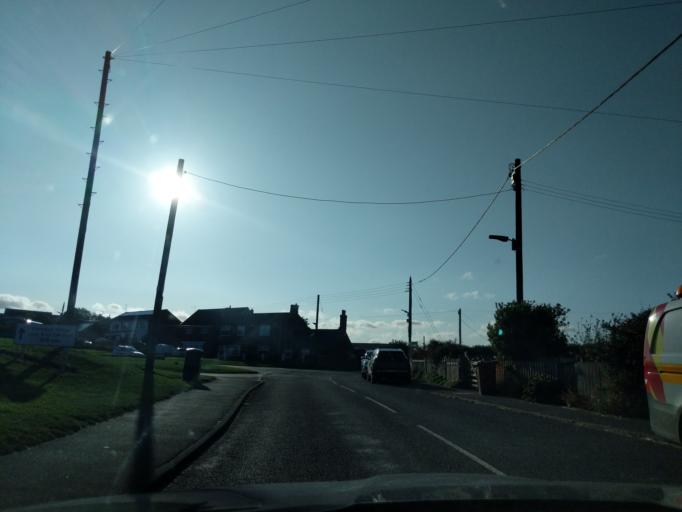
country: GB
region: England
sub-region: Northumberland
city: Cresswell
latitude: 55.2354
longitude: -1.5391
